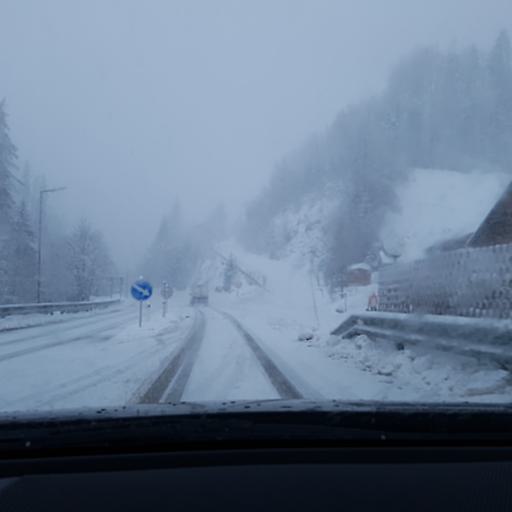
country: AT
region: Salzburg
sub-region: Politischer Bezirk Hallein
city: Abtenau
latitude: 47.5896
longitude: 13.4619
